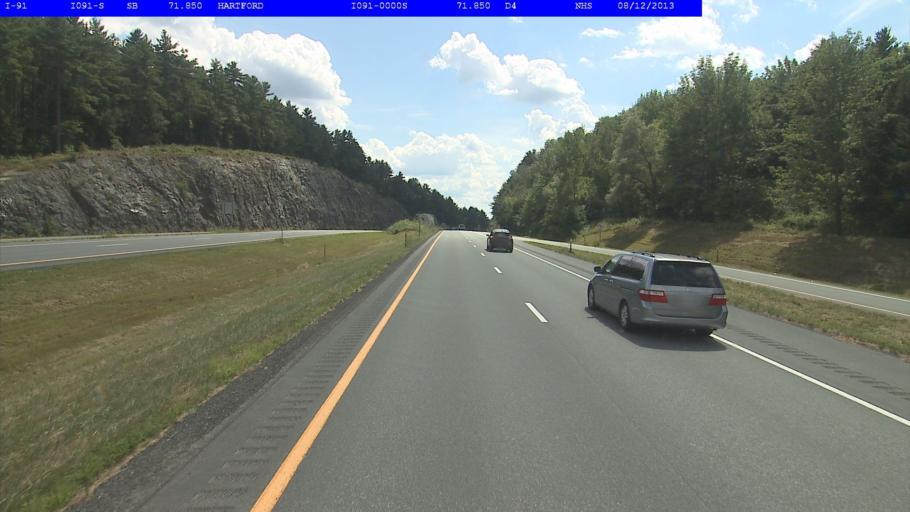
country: US
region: Vermont
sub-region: Windsor County
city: Wilder
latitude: 43.6643
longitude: -72.3200
